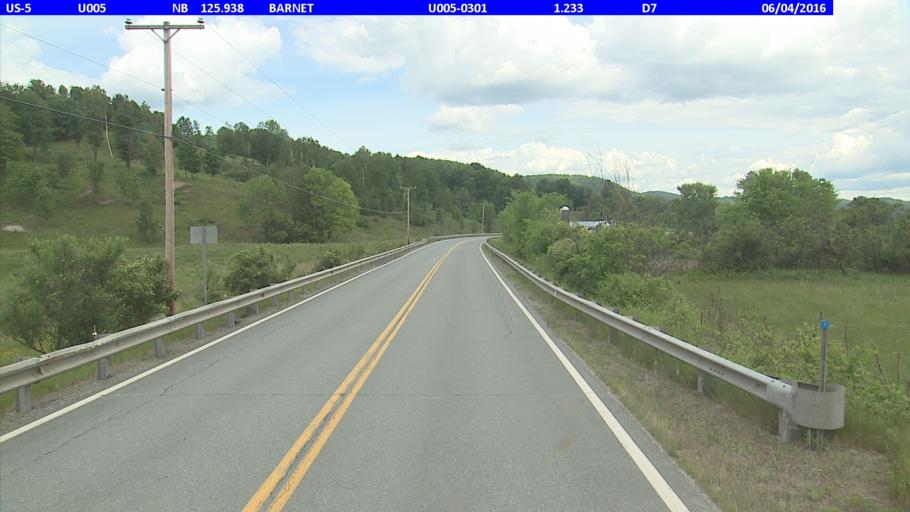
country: US
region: New Hampshire
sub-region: Grafton County
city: Woodsville
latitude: 44.2729
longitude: -72.0692
